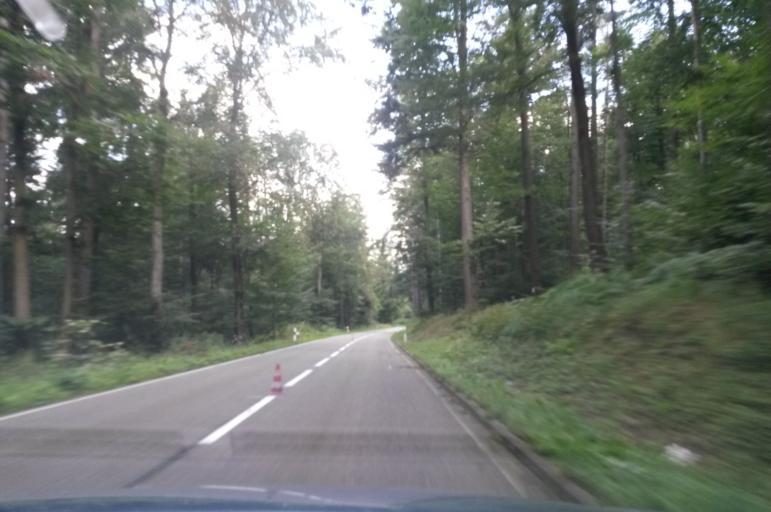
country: DE
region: Baden-Wuerttemberg
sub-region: Karlsruhe Region
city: Bad Herrenalb
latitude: 48.8643
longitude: 8.4522
